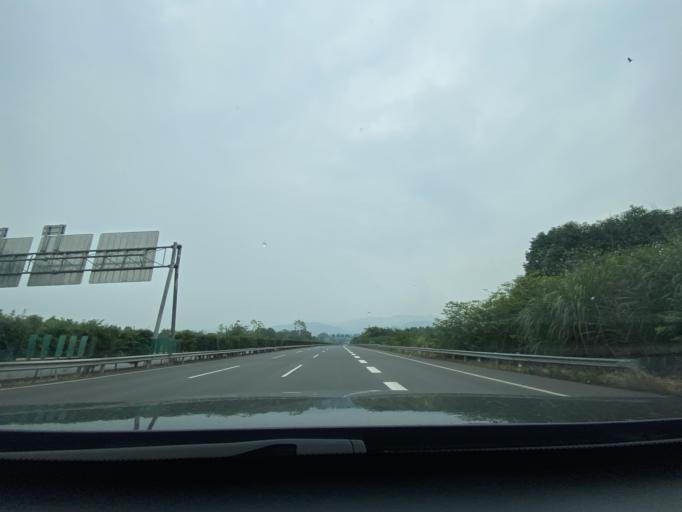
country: CN
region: Sichuan
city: Longquan
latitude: 30.3455
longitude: 104.1287
